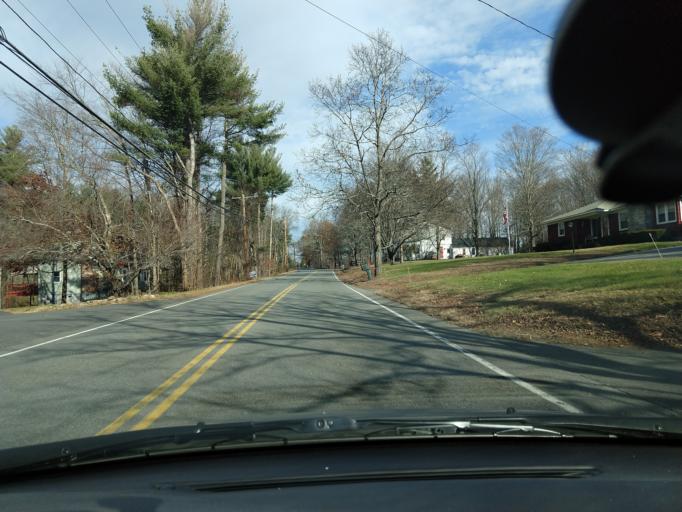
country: US
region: Massachusetts
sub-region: Middlesex County
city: East Pepperell
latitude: 42.6786
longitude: -71.5671
